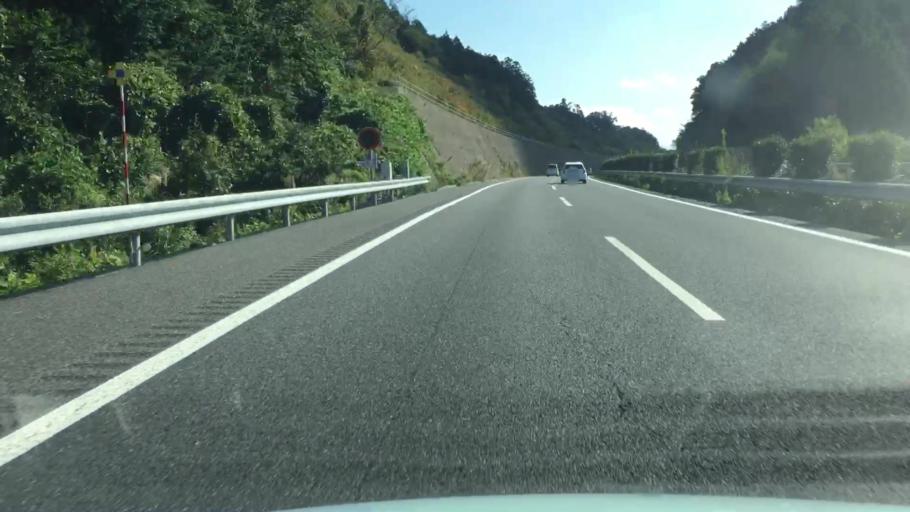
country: JP
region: Ibaraki
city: Iwase
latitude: 36.3484
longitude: 140.1616
